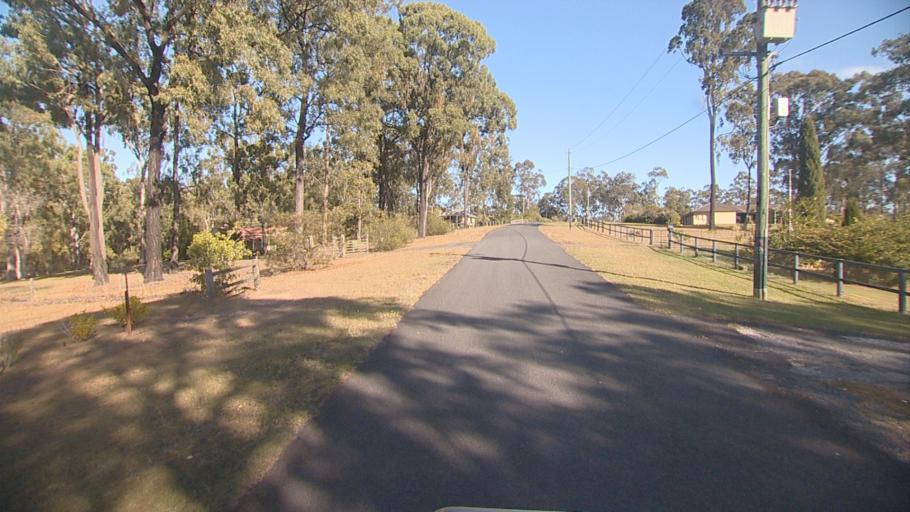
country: AU
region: Queensland
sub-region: Ipswich
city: Springfield Lakes
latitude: -27.7005
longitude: 152.9318
